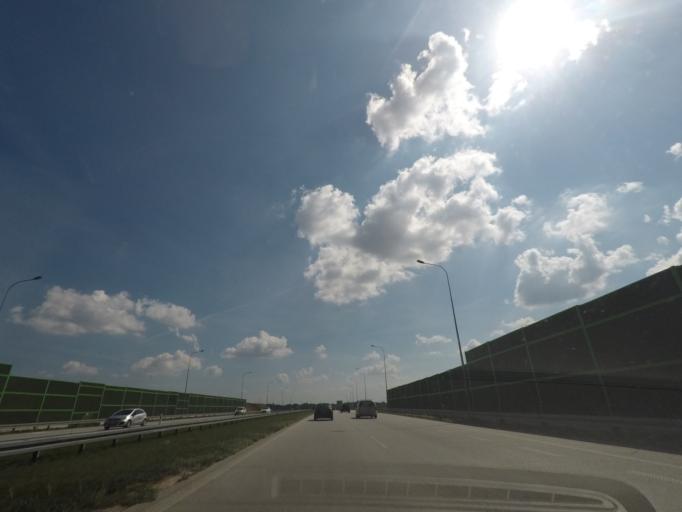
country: PL
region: Lodz Voivodeship
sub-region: Powiat zgierski
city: Strykow
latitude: 51.8459
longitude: 19.6597
